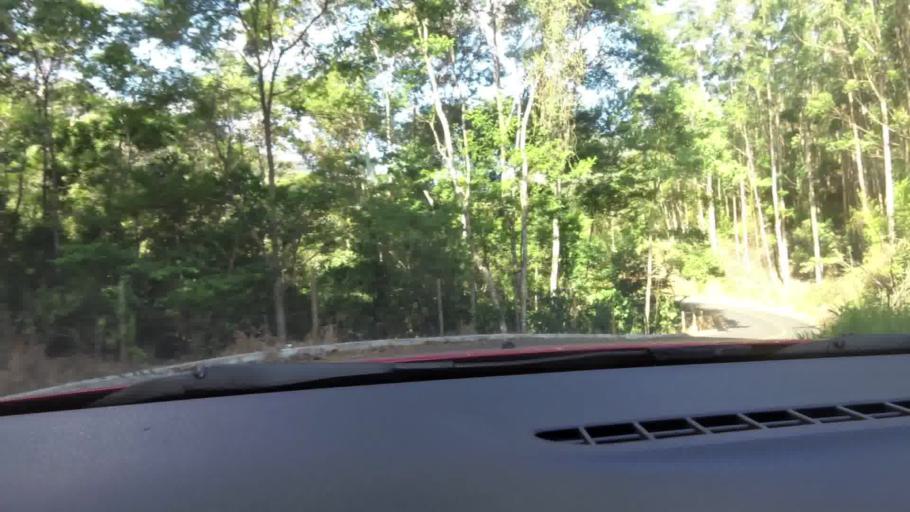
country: BR
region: Espirito Santo
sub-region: Guarapari
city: Guarapari
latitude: -20.5784
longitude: -40.5461
